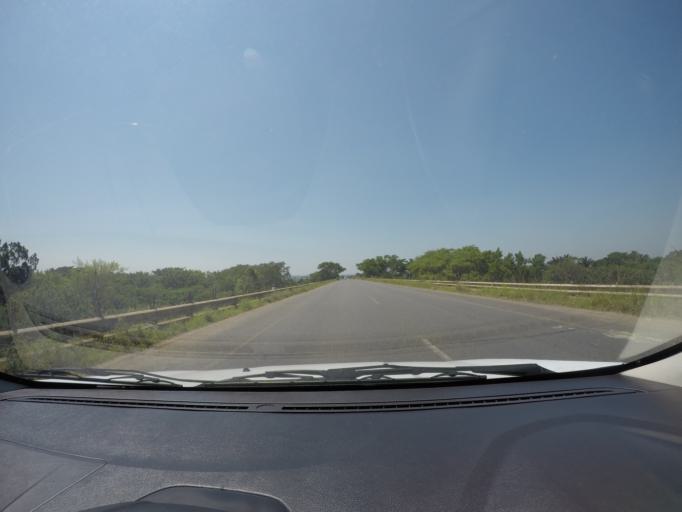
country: ZA
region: KwaZulu-Natal
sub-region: uThungulu District Municipality
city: Empangeni
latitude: -28.7999
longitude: 31.9583
